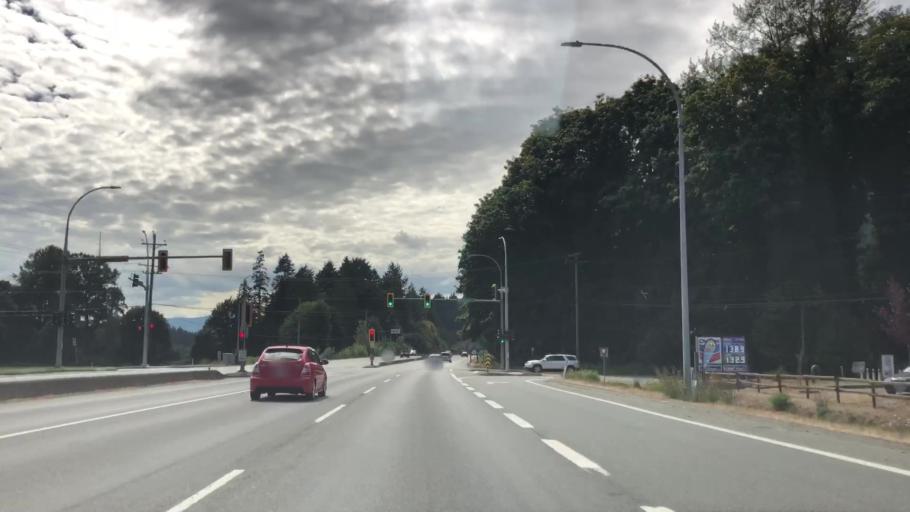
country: CA
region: British Columbia
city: North Cowichan
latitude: 48.8753
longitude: -123.7067
